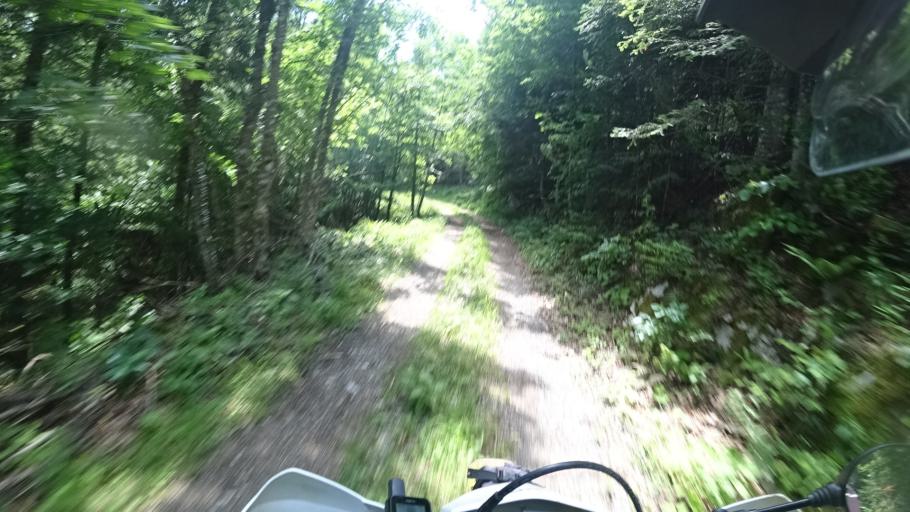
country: SI
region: Osilnica
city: Osilnica
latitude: 45.4898
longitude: 14.7185
